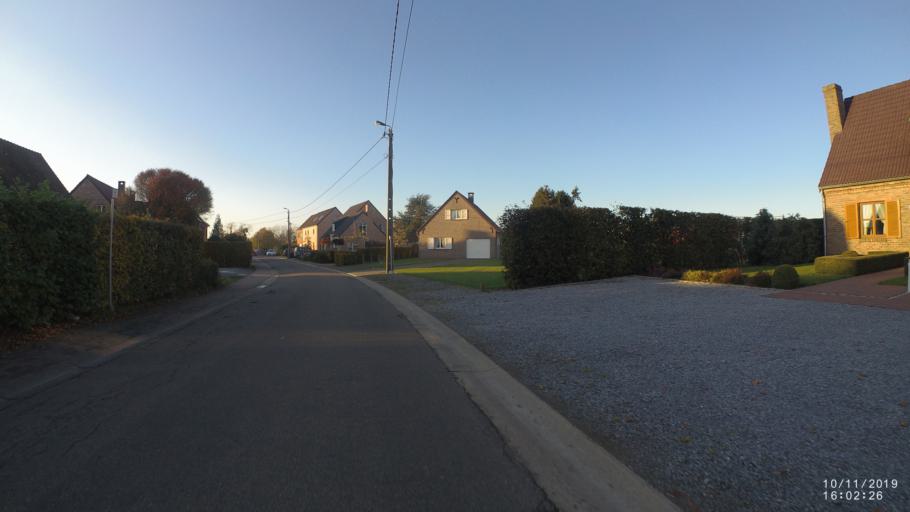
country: BE
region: Flanders
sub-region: Provincie Vlaams-Brabant
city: Lubbeek
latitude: 50.9036
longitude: 4.8699
